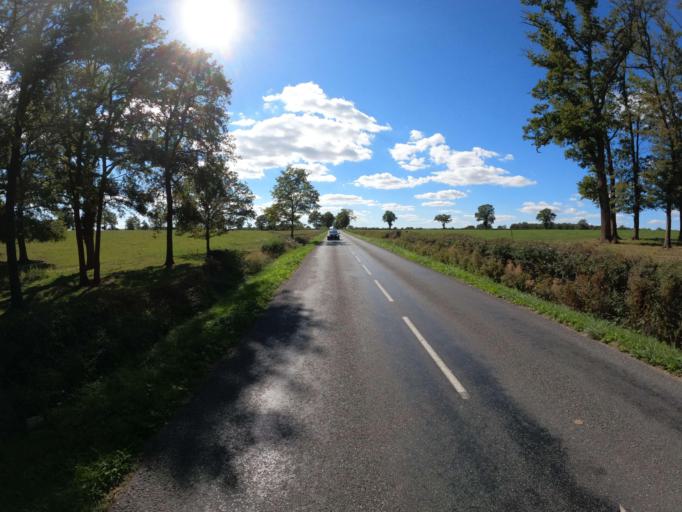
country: FR
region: Auvergne
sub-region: Departement de l'Allier
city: Doyet
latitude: 46.3901
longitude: 2.8067
